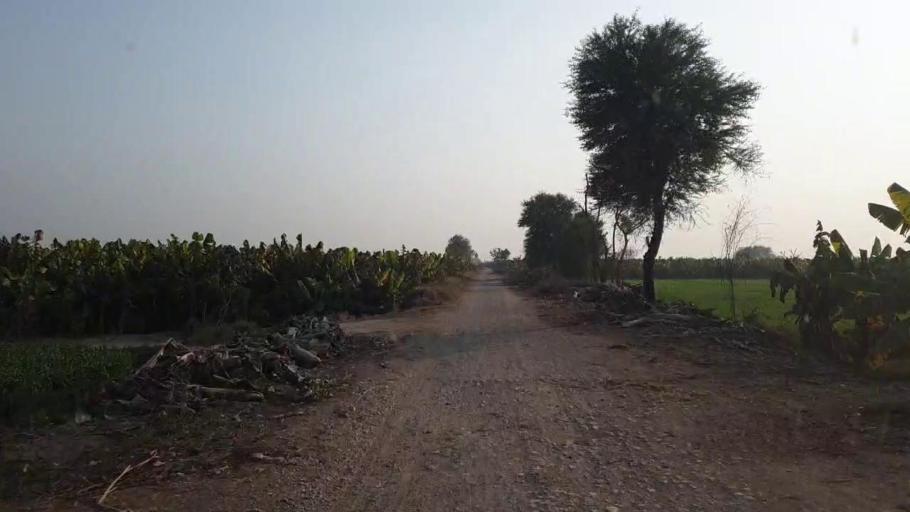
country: PK
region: Sindh
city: Hala
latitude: 25.8932
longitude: 68.4498
